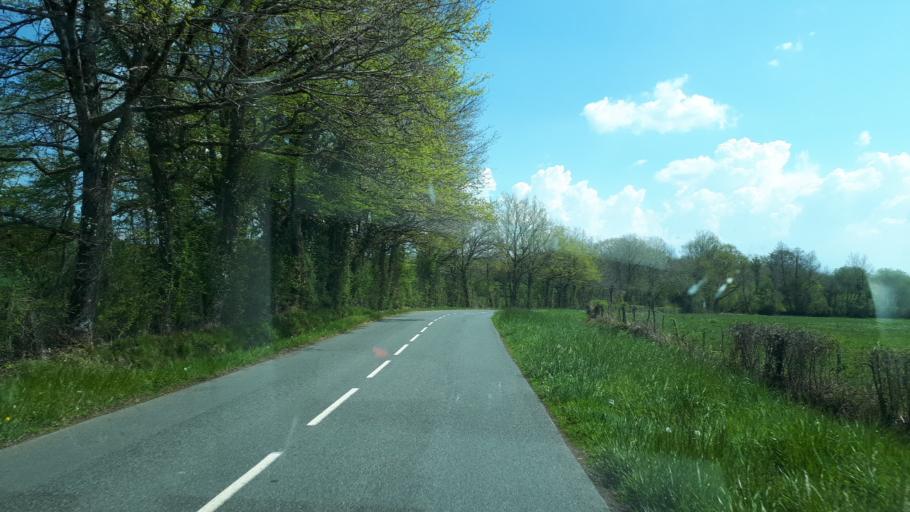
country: FR
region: Centre
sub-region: Departement du Cher
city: Henrichemont
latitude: 47.3051
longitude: 2.6476
